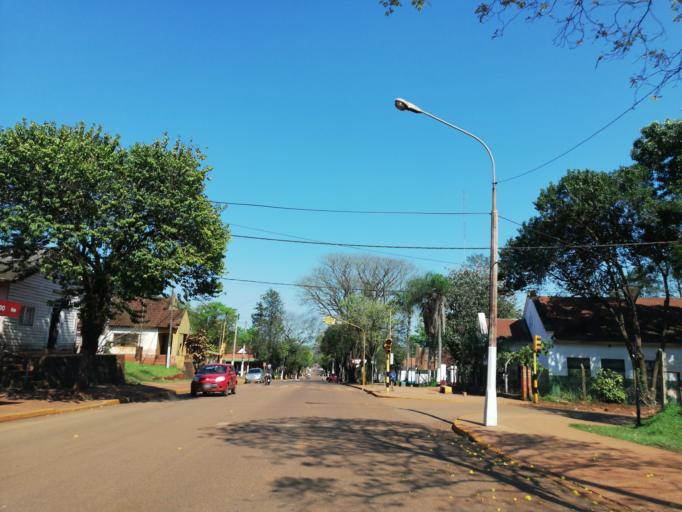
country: AR
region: Misiones
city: Puerto Eldorado
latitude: -26.4078
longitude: -54.6703
